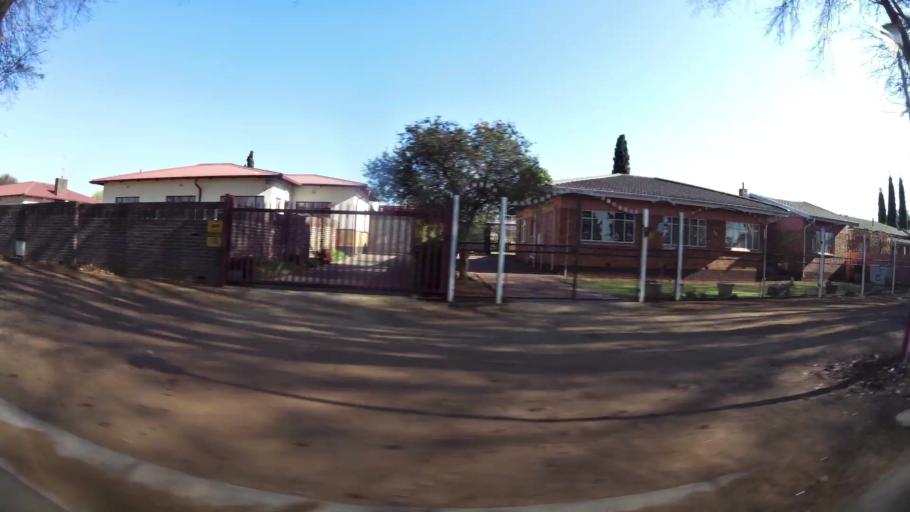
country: ZA
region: Gauteng
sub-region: Ekurhuleni Metropolitan Municipality
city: Benoni
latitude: -26.1610
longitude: 28.3152
